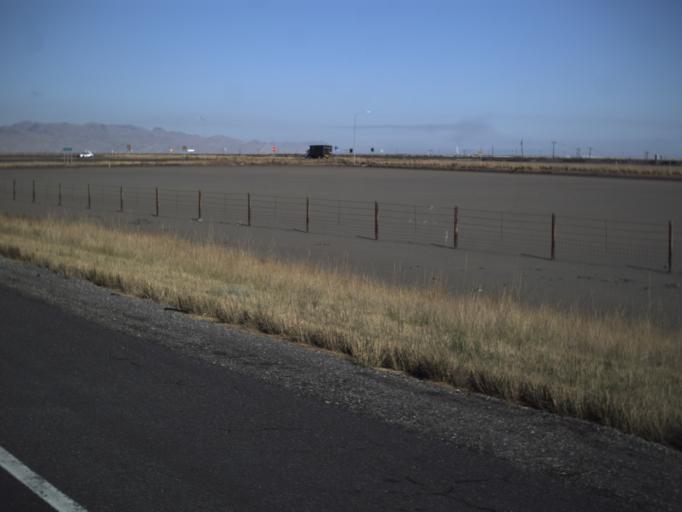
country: US
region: Utah
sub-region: Tooele County
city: Grantsville
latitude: 40.7066
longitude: -112.5192
